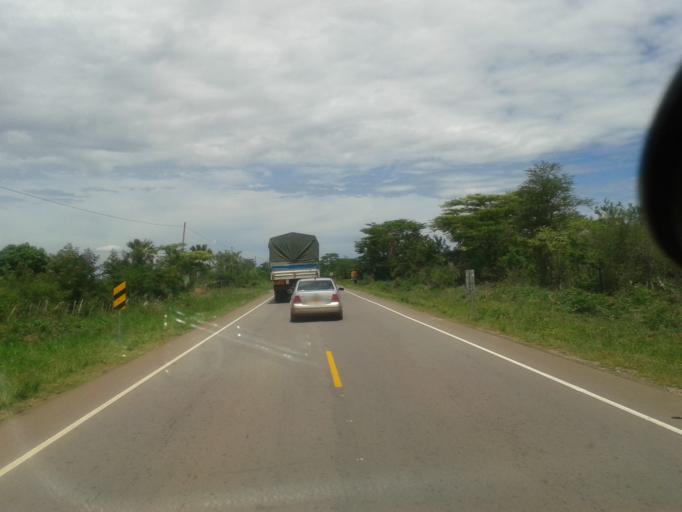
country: UG
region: Western Region
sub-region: Kiryandongo District
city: Masindi Port
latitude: 1.6445
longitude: 32.0313
